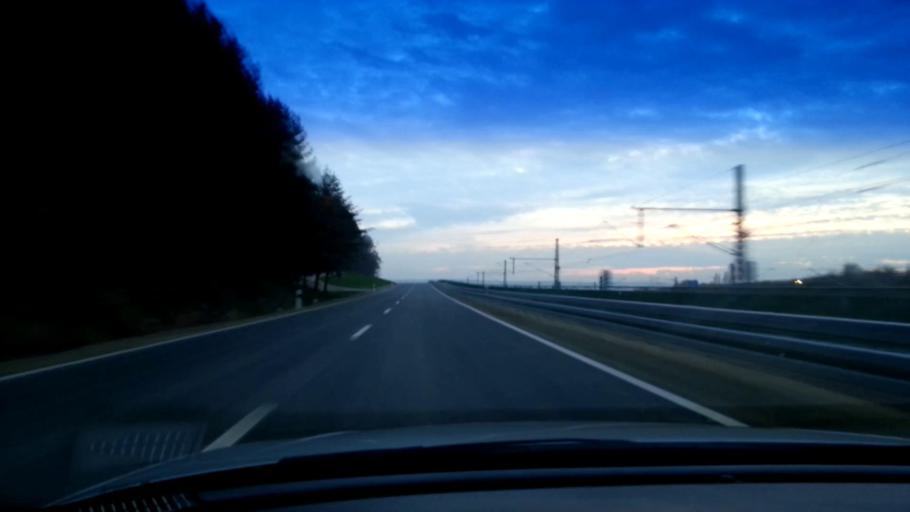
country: DE
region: Bavaria
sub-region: Upper Franconia
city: Breitengussbach
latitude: 49.9864
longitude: 10.9002
